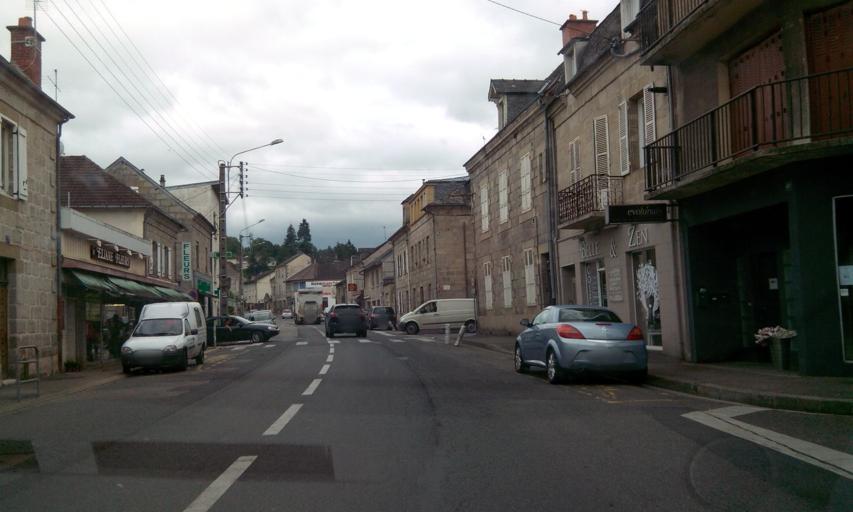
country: FR
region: Limousin
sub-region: Departement de la Correze
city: Brive-la-Gaillarde
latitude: 45.1529
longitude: 1.5397
